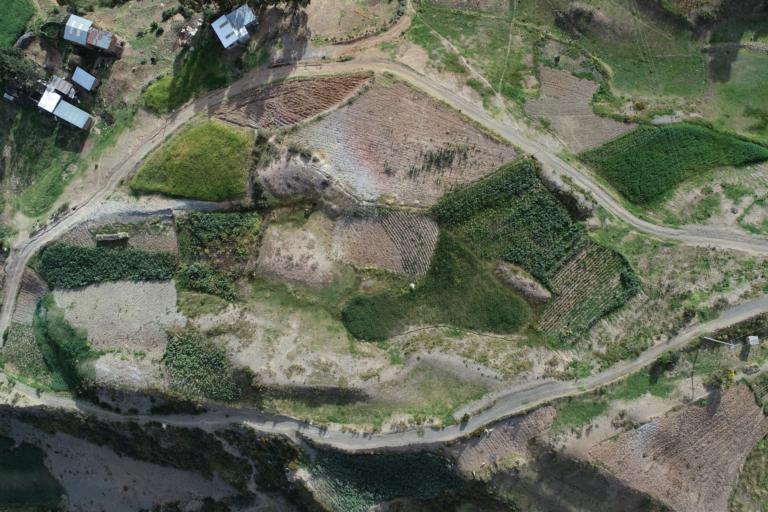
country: BO
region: La Paz
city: La Paz
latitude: -16.5480
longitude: -68.0003
